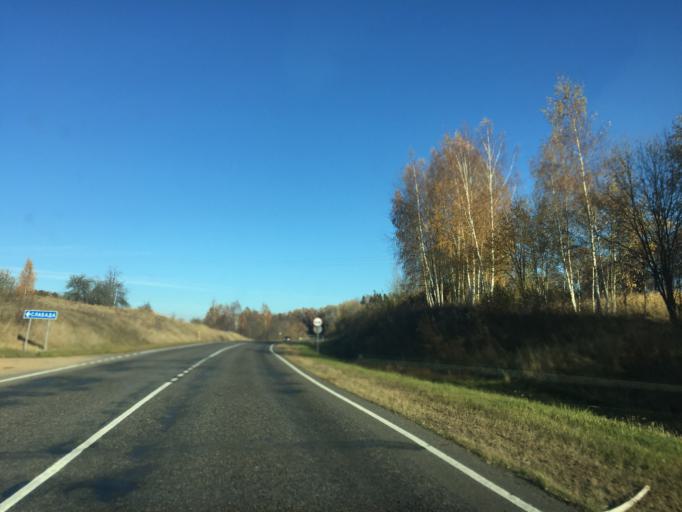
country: BY
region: Vitebsk
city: Navapolatsk
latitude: 55.3773
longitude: 28.4042
